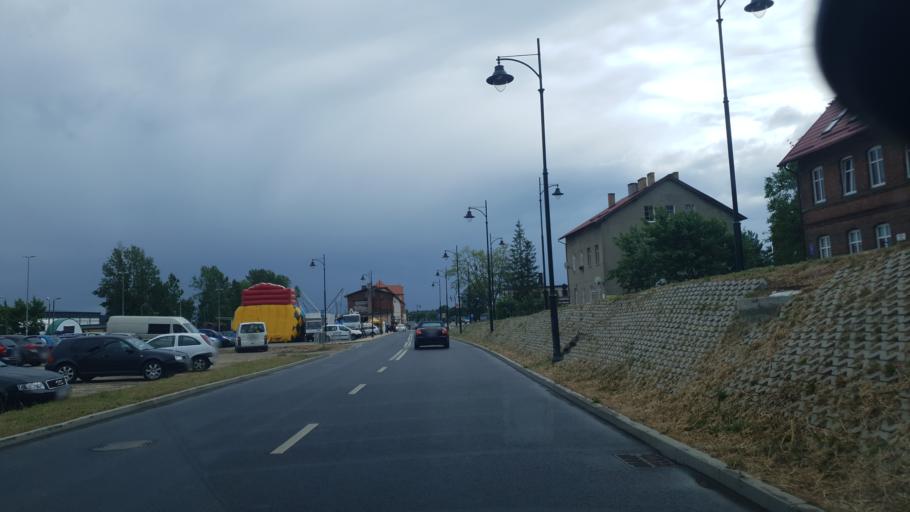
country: PL
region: Pomeranian Voivodeship
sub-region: Powiat kartuski
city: Kartuzy
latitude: 54.3360
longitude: 18.2067
